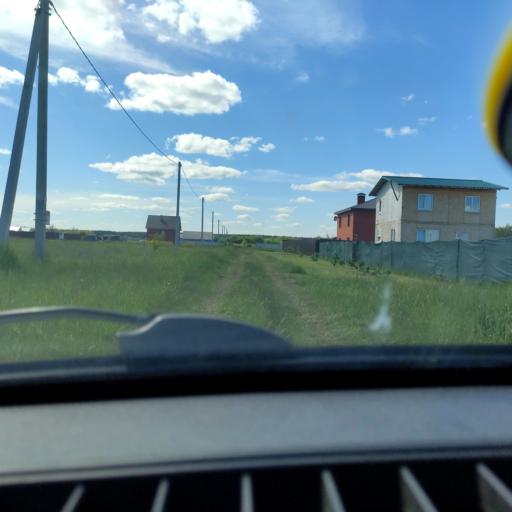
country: RU
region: Samara
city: Podstepki
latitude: 53.5236
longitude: 49.1052
